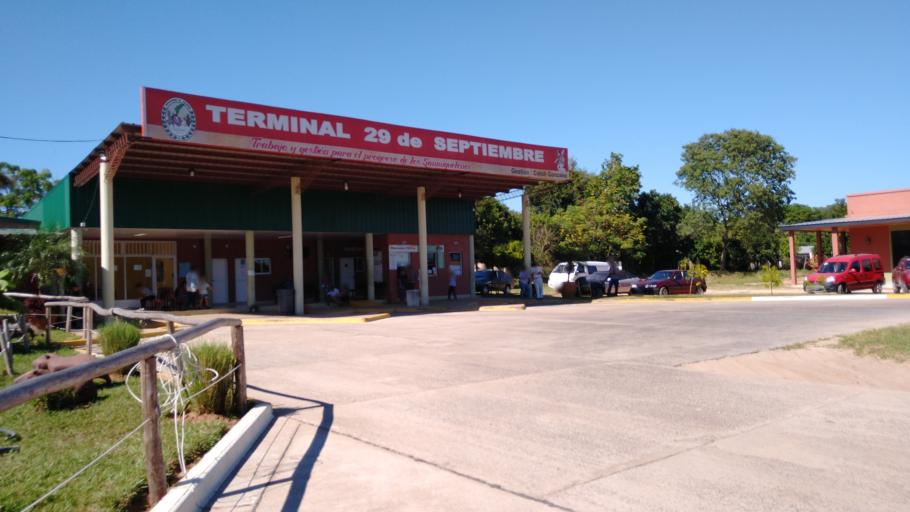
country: AR
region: Corrientes
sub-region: Departamento de San Miguel
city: San Miguel
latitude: -27.9922
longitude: -57.5960
